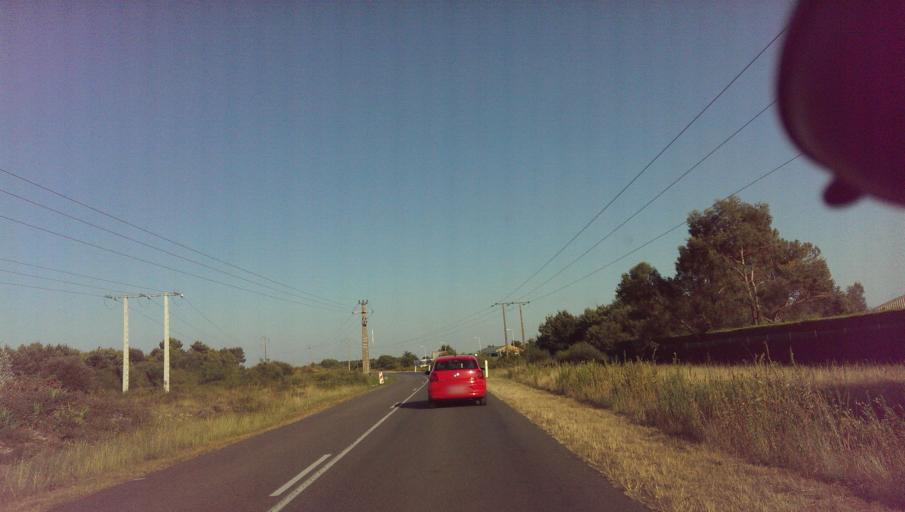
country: FR
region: Aquitaine
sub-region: Departement des Landes
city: Mimizan
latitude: 44.1883
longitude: -1.2097
